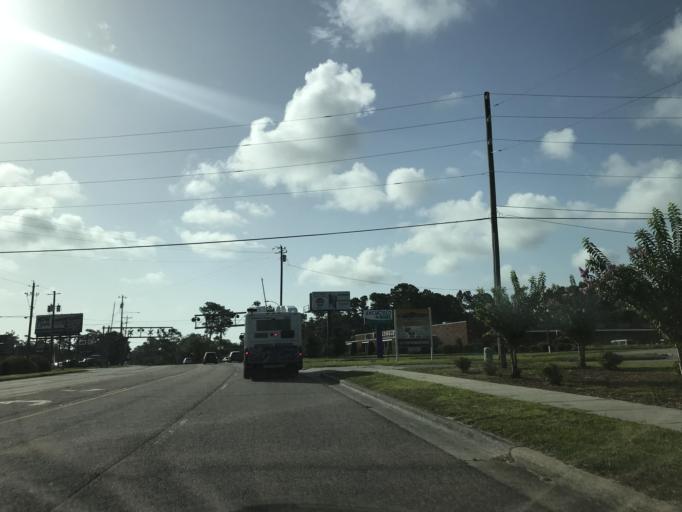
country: US
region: North Carolina
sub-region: New Hanover County
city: Wilmington
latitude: 34.2251
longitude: -77.9233
